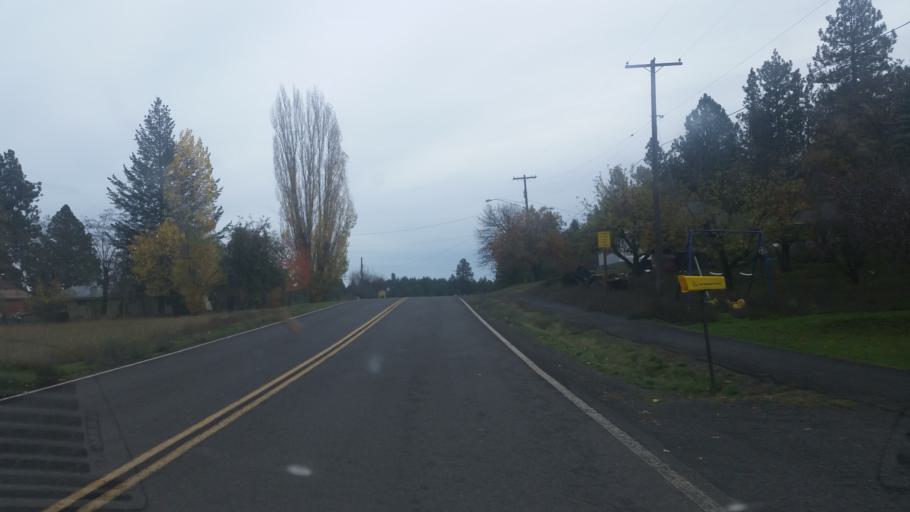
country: US
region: Washington
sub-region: Spokane County
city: Cheney
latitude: 47.2298
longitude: -117.4638
